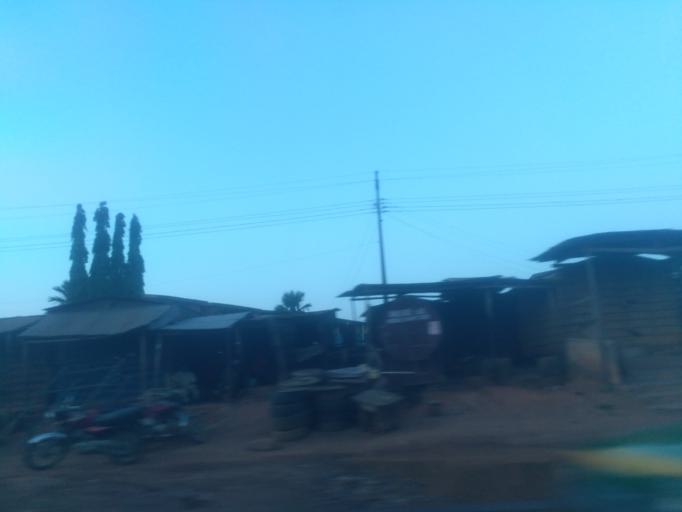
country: NG
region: Ogun
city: Abeokuta
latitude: 7.1789
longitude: 3.4015
